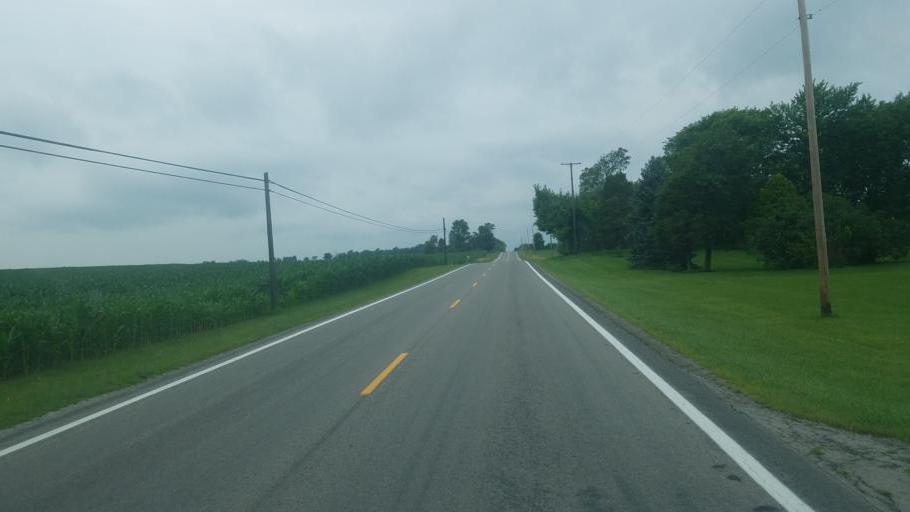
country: US
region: Ohio
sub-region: Hardin County
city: Kenton
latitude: 40.6089
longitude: -83.6933
